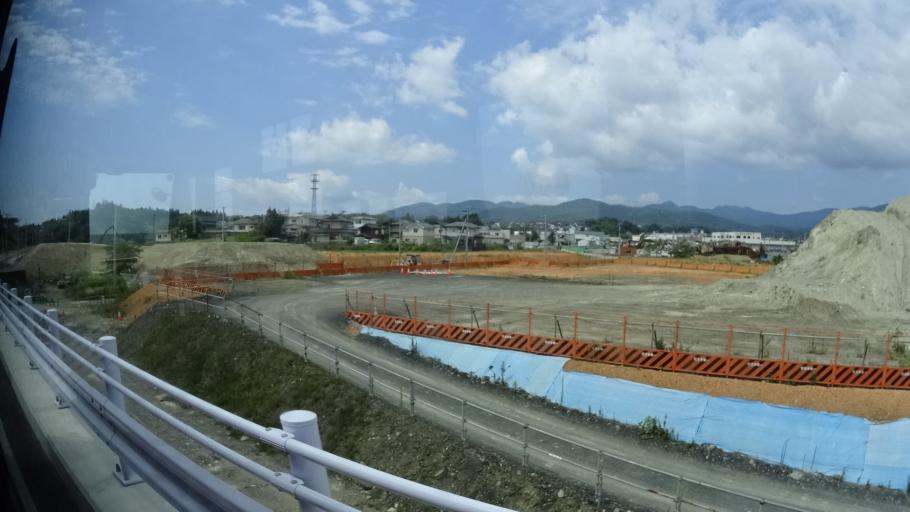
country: JP
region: Iwate
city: Ofunato
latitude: 38.8699
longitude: 141.5847
